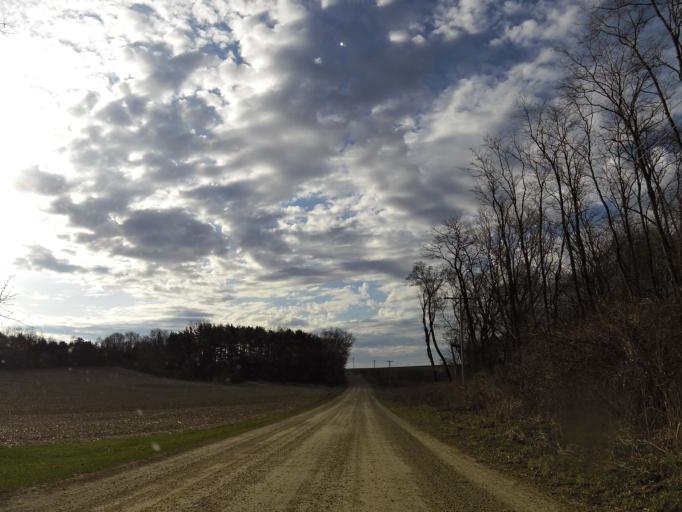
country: US
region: Minnesota
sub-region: Dakota County
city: Hastings
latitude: 44.7663
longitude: -92.8380
